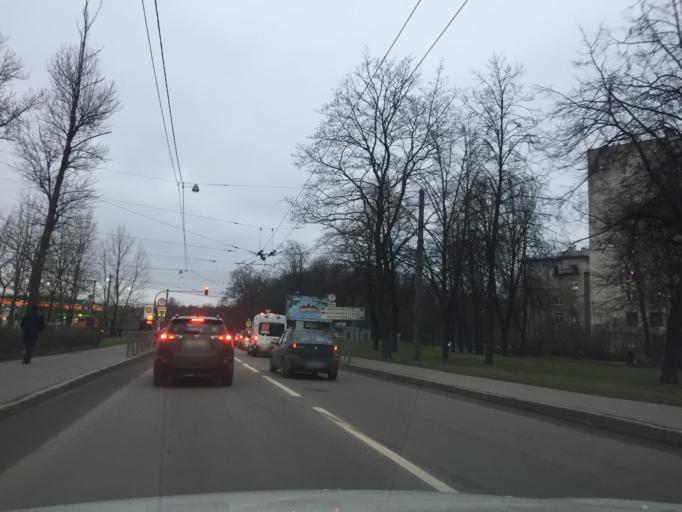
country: RU
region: St.-Petersburg
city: Kushelevka
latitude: 59.9953
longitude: 30.3564
